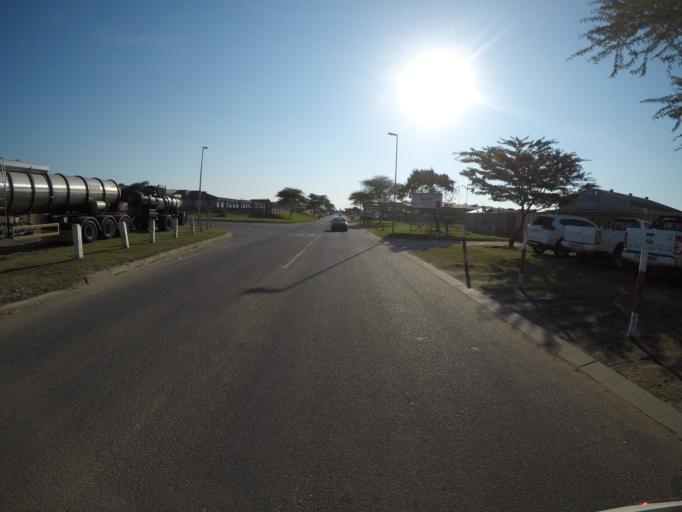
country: ZA
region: KwaZulu-Natal
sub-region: uThungulu District Municipality
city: Richards Bay
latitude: -28.7406
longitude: 32.0378
